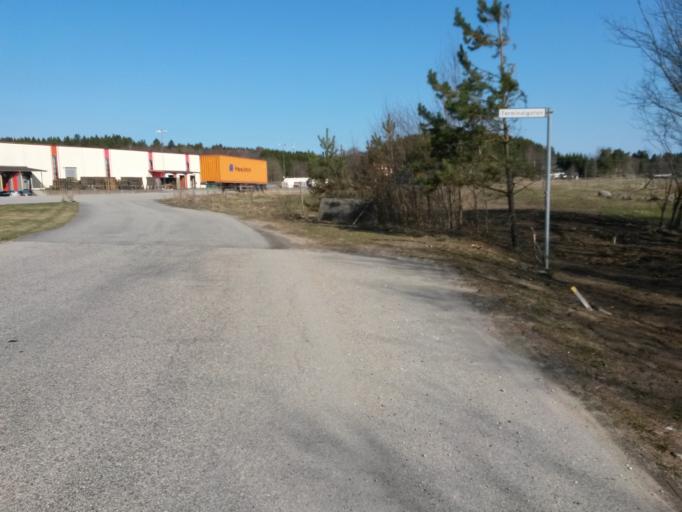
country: SE
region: Vaestra Goetaland
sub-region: Vargarda Kommun
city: Vargarda
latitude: 58.0431
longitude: 12.8074
